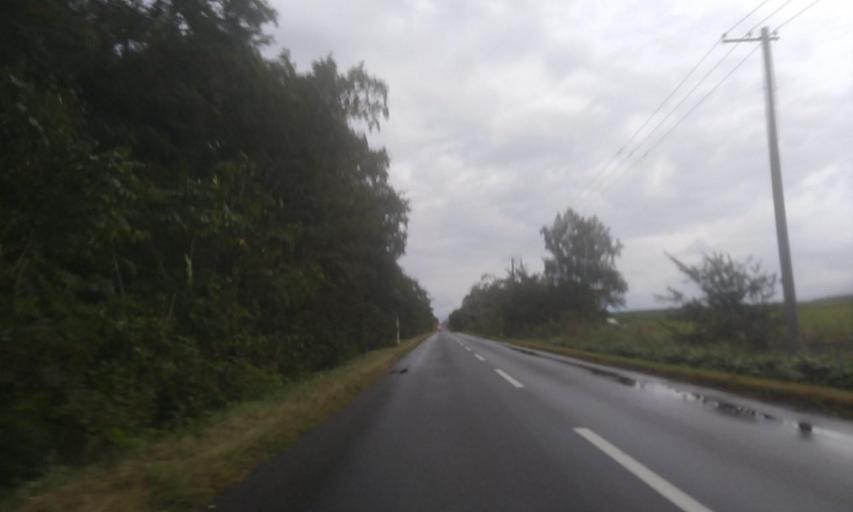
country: JP
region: Hokkaido
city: Abashiri
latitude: 43.8912
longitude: 144.4552
